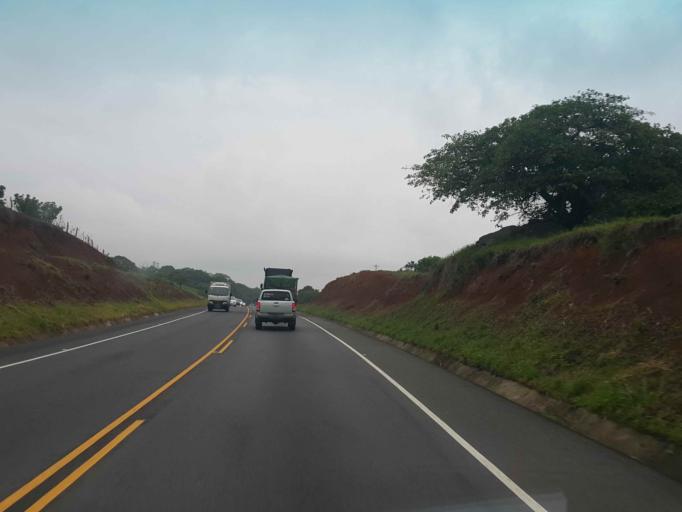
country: CR
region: Alajuela
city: Carrillos
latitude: 9.9639
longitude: -84.2901
